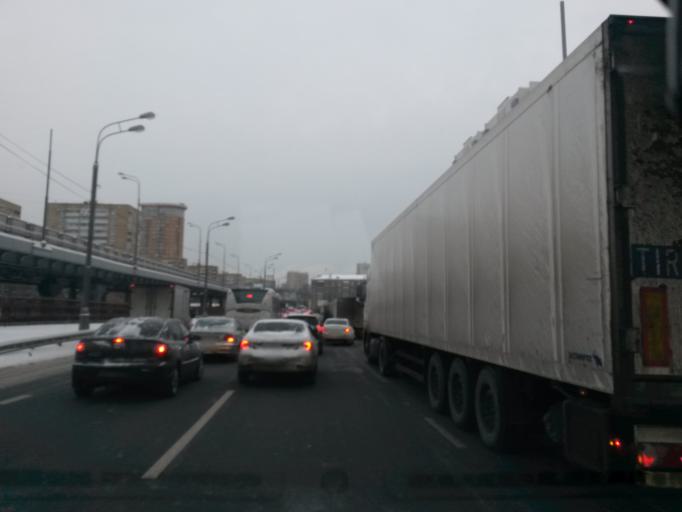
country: RU
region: Moskovskaya
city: Bol'shaya Setun'
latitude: 55.7189
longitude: 37.4200
